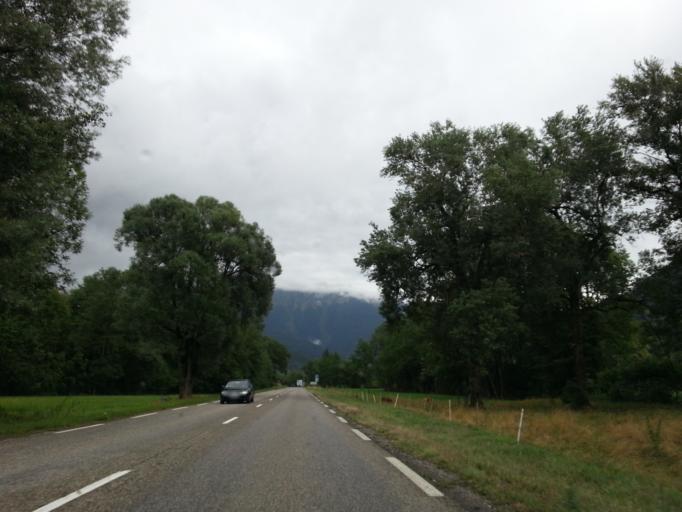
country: FR
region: Rhone-Alpes
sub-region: Departement de la Haute-Savoie
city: Faverges
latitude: 45.7590
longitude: 6.2644
